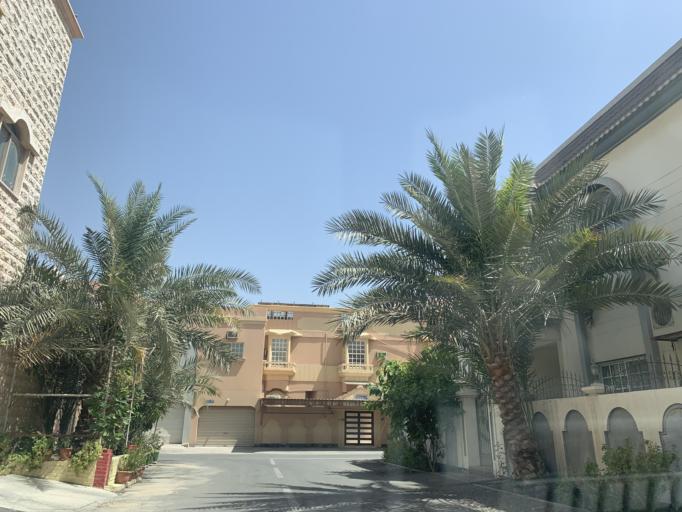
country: BH
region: Northern
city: Sitrah
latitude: 26.1577
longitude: 50.6089
